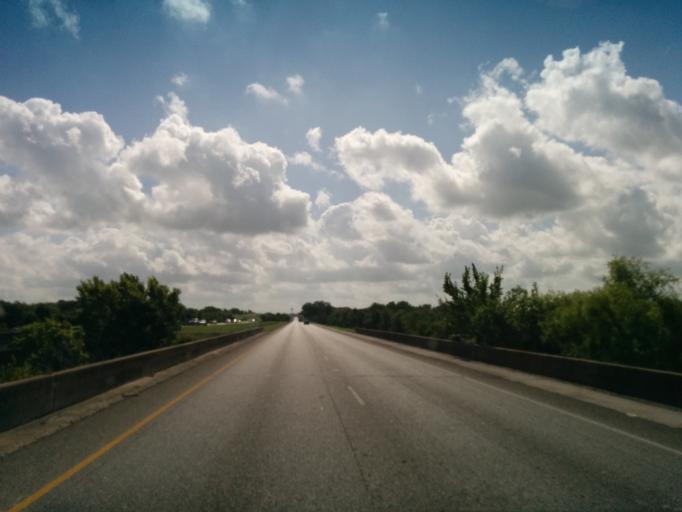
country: US
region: Texas
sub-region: Fayette County
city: Schulenburg
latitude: 29.6893
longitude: -96.9429
